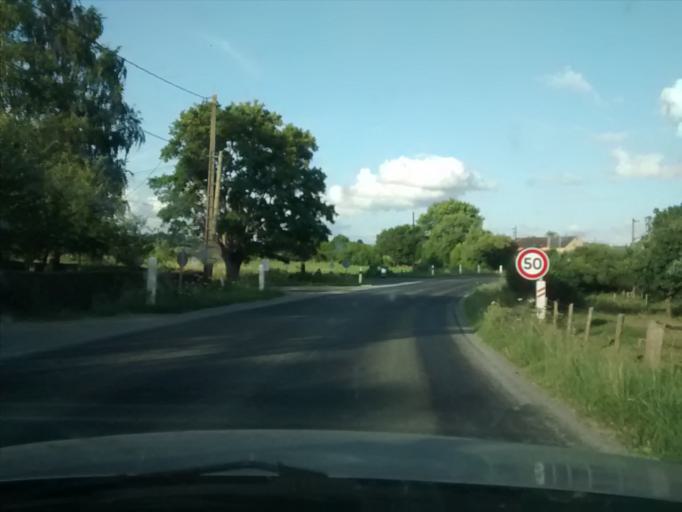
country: FR
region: Pays de la Loire
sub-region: Departement de la Mayenne
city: Montsurs
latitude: 48.1529
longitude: -0.4935
